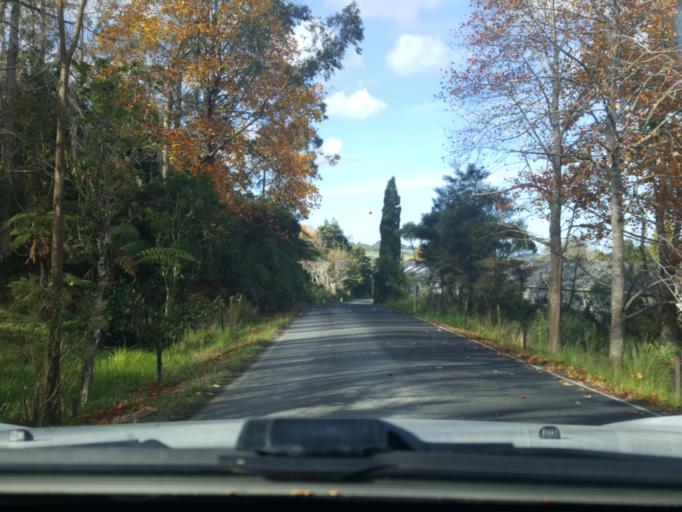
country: NZ
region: Auckland
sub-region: Auckland
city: Muriwai Beach
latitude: -36.7473
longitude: 174.4290
